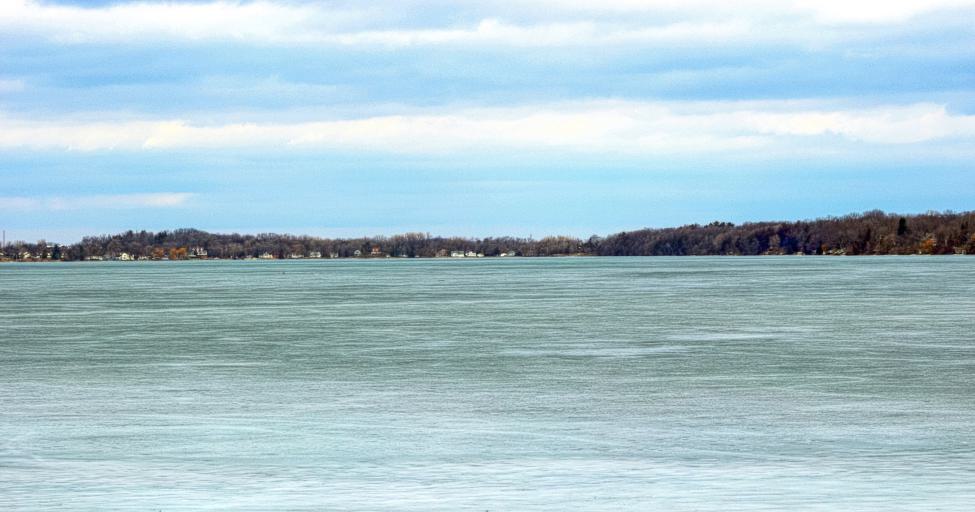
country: US
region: Wisconsin
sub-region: Jefferson County
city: Lake Mills
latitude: 43.0667
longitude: -88.9292
